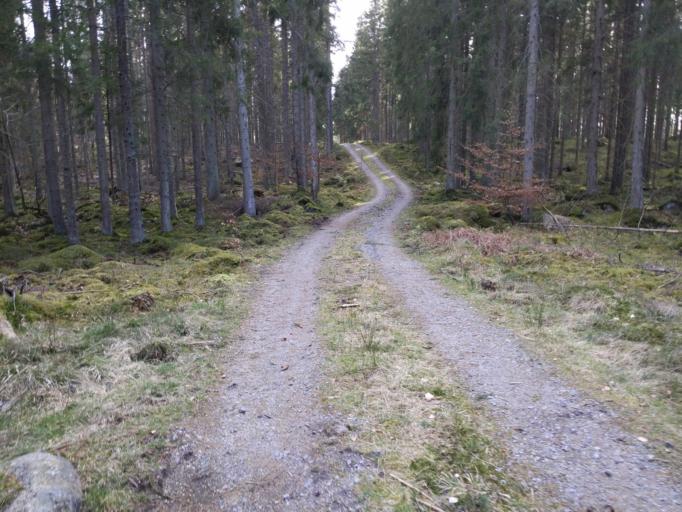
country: SE
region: Blekinge
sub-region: Karlshamns Kommun
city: Svangsta
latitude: 56.4125
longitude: 14.7791
